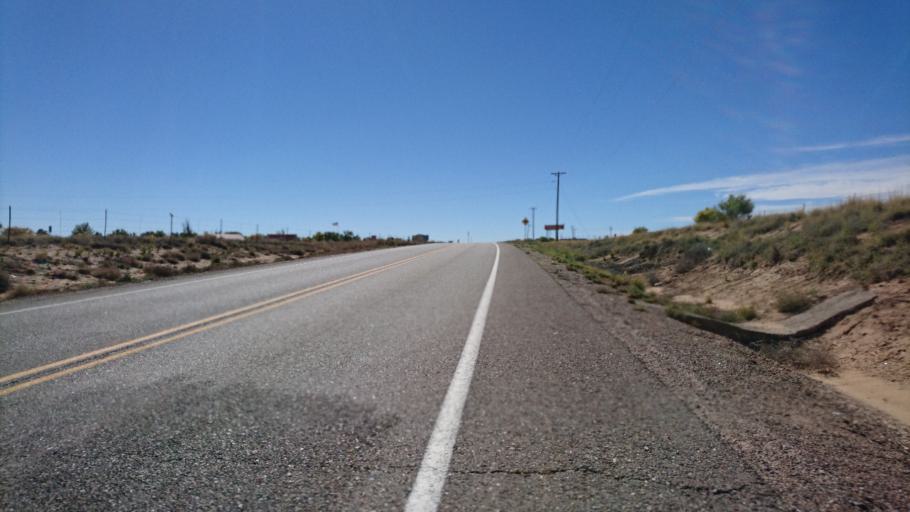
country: US
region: New Mexico
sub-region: Bernalillo County
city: South Valley
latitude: 35.0634
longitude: -106.7953
